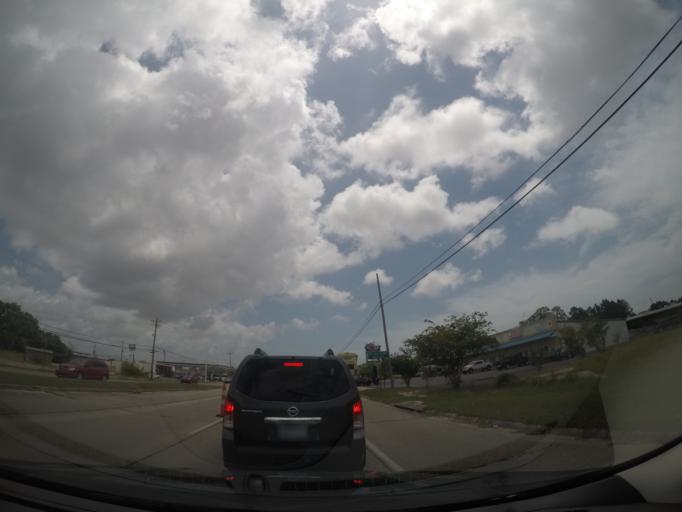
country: US
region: Mississippi
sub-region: Hancock County
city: Bay Saint Louis
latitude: 30.3162
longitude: -89.3485
